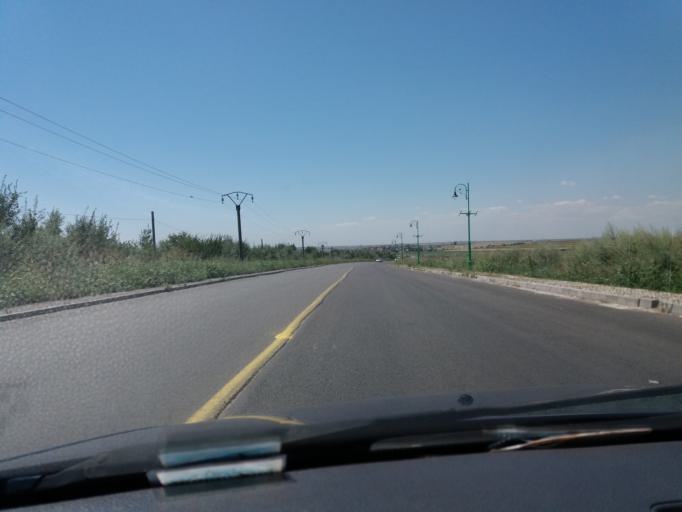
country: RO
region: Constanta
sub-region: Comuna Navodari
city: Navodari
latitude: 44.2891
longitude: 28.6076
